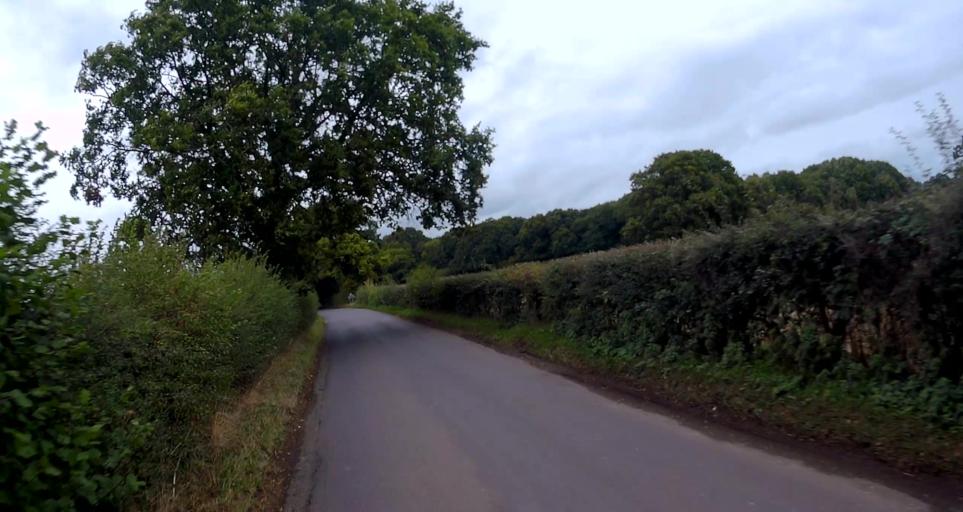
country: GB
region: England
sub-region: Hampshire
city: Four Marks
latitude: 51.1393
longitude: -1.0831
